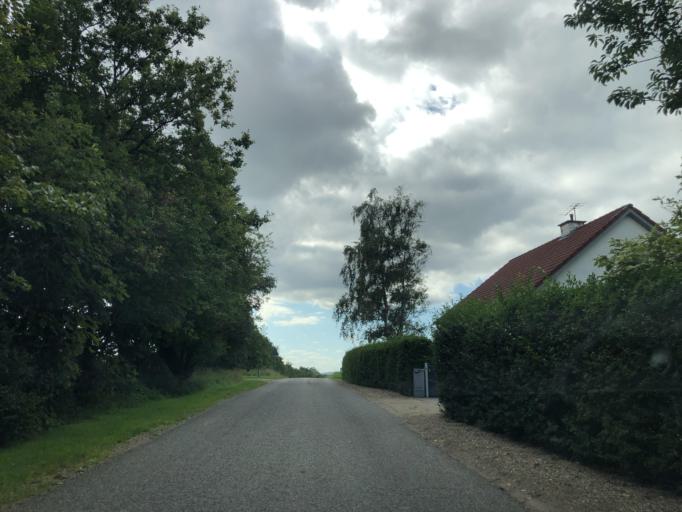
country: DK
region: North Denmark
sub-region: Vesthimmerland Kommune
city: Alestrup
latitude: 56.5916
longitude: 9.4055
